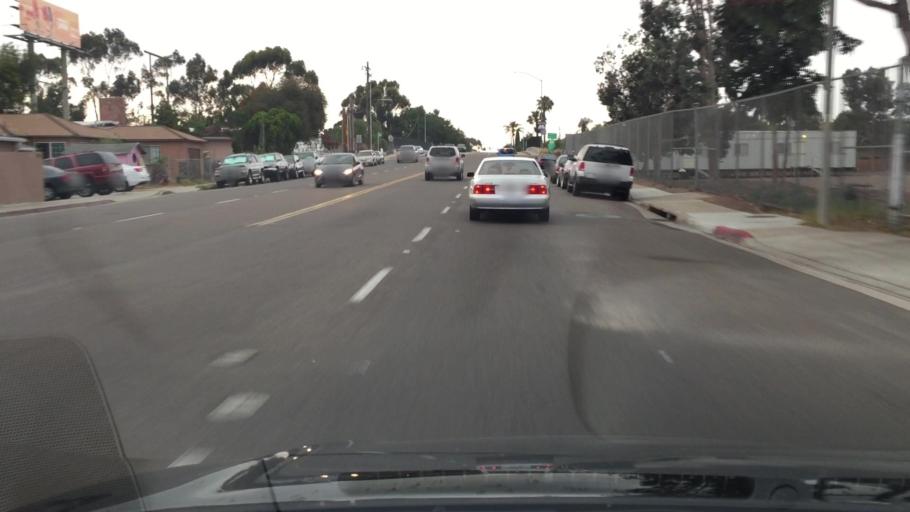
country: US
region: California
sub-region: San Diego County
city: National City
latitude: 32.7168
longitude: -117.0936
